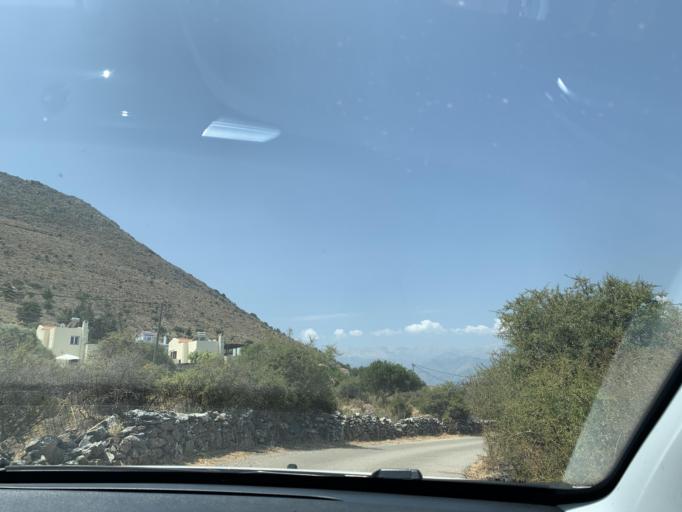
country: GR
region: Crete
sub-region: Nomos Chanias
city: Kalivai
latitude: 35.4515
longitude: 24.2324
